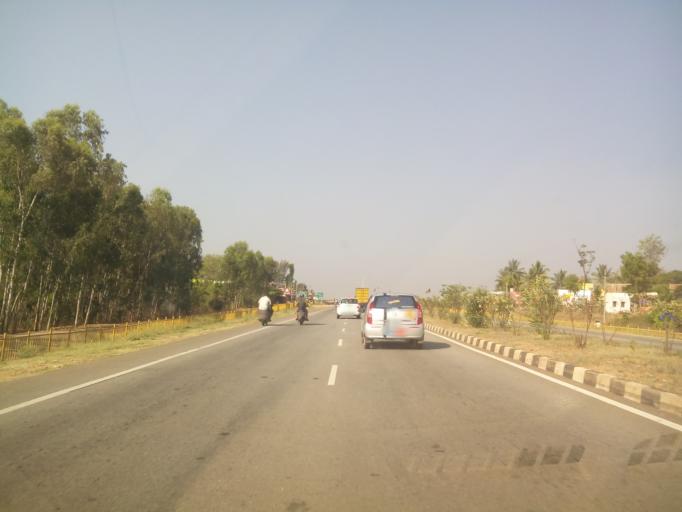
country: IN
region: Karnataka
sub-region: Ramanagara
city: Magadi
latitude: 13.0586
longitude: 77.1616
